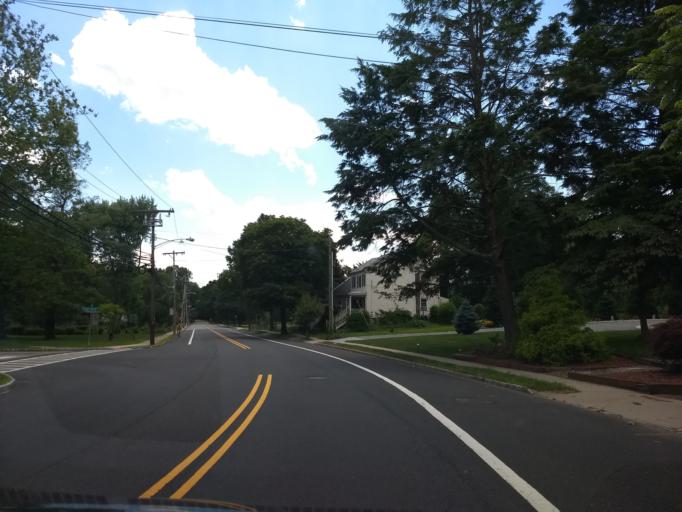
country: US
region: New Jersey
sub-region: Morris County
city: Morristown
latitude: 40.7880
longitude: -74.4787
